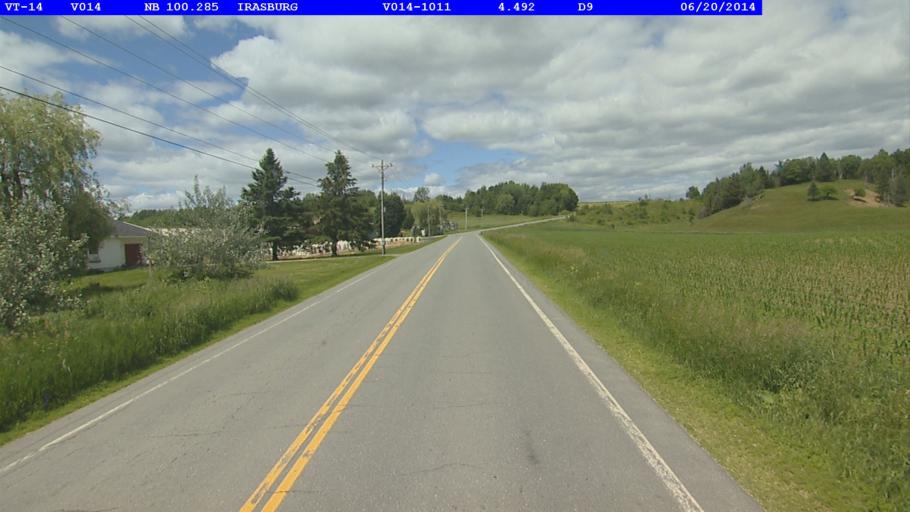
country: US
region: Vermont
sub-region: Orleans County
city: Newport
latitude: 44.8246
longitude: -72.2948
